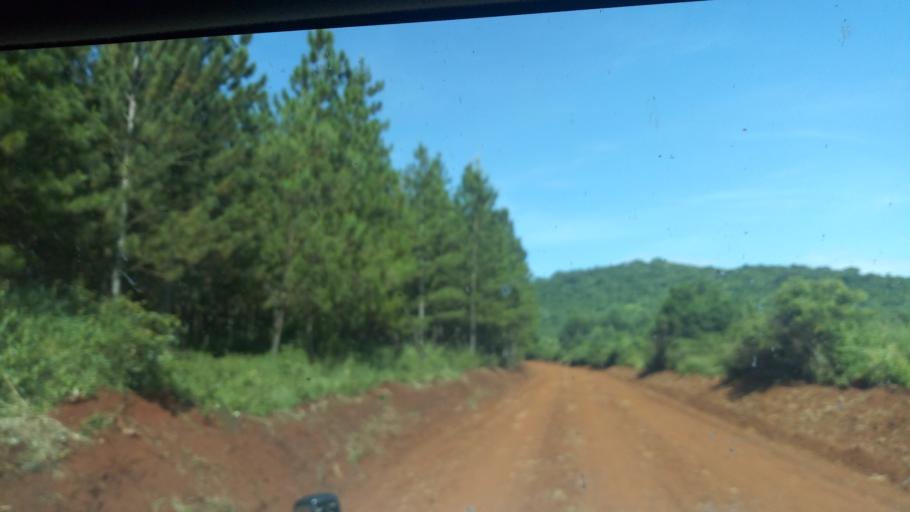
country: UG
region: Western Region
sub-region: Masindi District
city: Masindi
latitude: 1.6505
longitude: 31.7798
